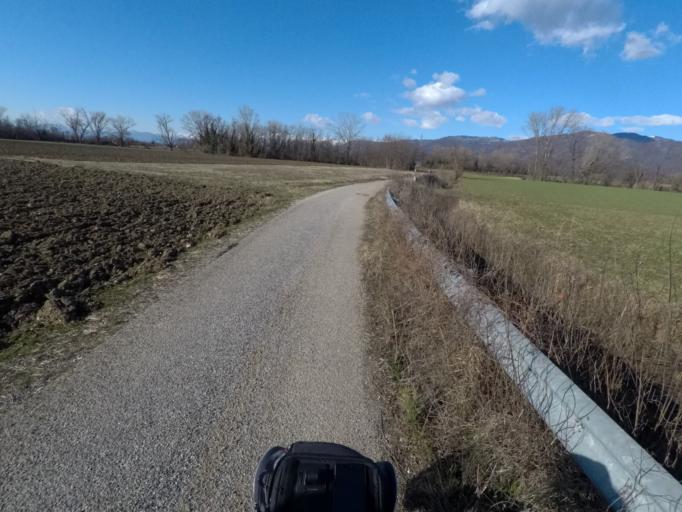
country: IT
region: Friuli Venezia Giulia
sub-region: Provincia di Udine
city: Moimacco
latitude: 46.0983
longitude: 13.3888
